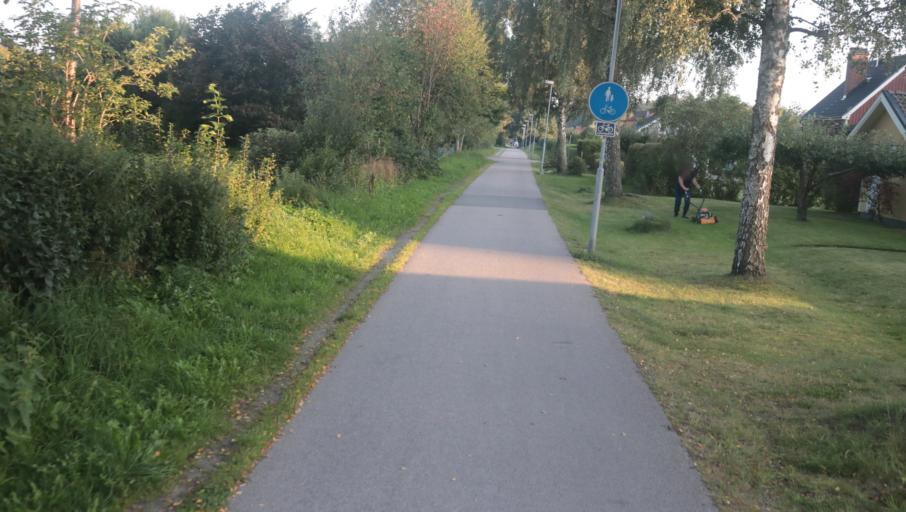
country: SE
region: Blekinge
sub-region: Karlshamns Kommun
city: Karlshamn
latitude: 56.1974
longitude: 14.8366
